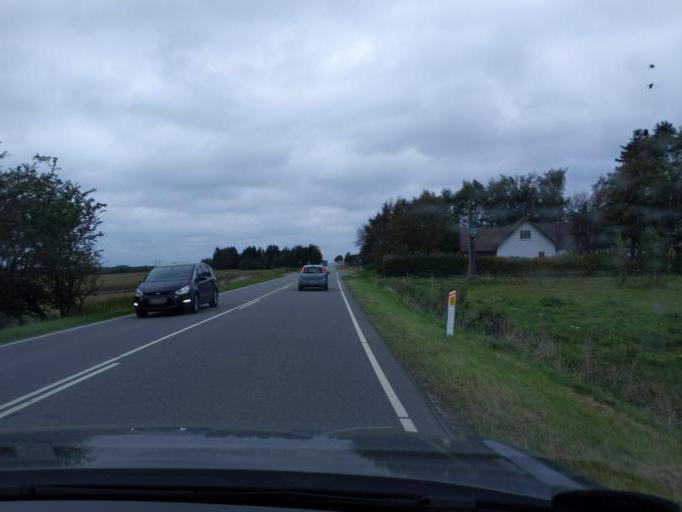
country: DK
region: North Denmark
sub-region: Mariagerfjord Kommune
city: Hobro
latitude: 56.5755
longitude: 9.8151
